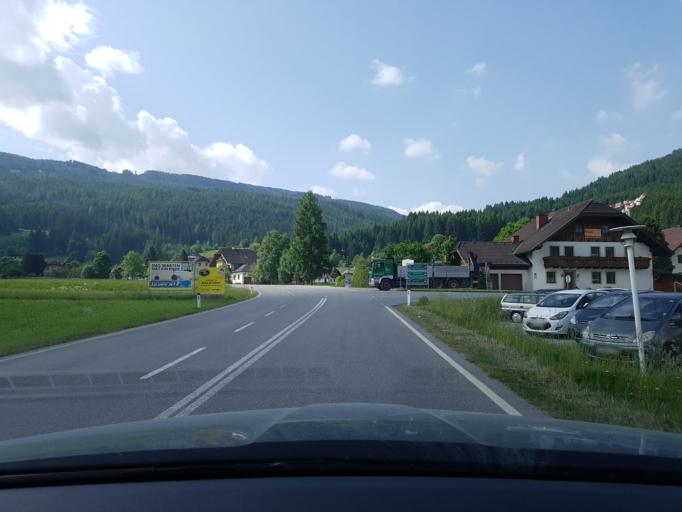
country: AT
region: Salzburg
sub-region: Politischer Bezirk Tamsweg
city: Sankt Margarethen im Lungau
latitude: 47.0828
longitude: 13.6922
